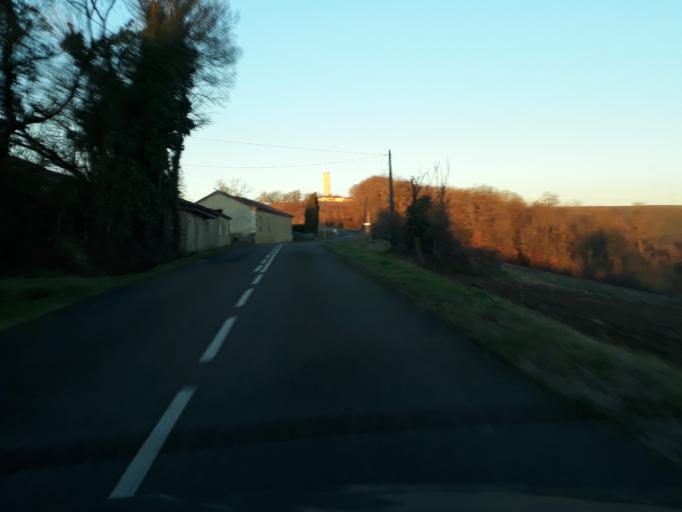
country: FR
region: Midi-Pyrenees
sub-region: Departement du Gers
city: Aubiet
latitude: 43.6008
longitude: 0.7044
